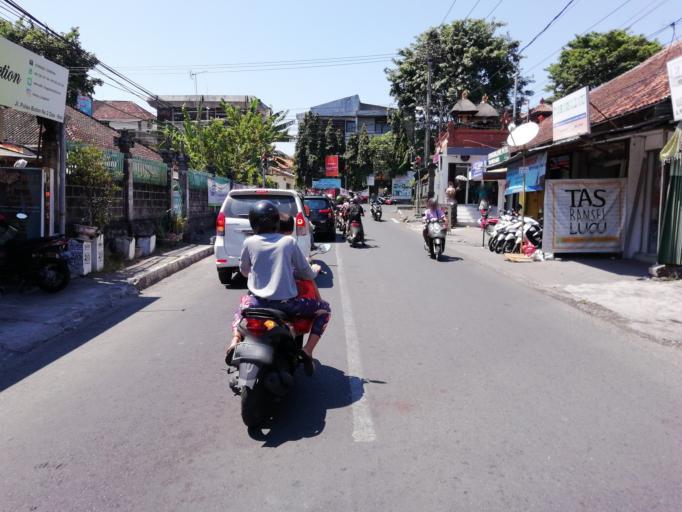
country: ID
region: Bali
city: Karyadharma
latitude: -8.6775
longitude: 115.2149
